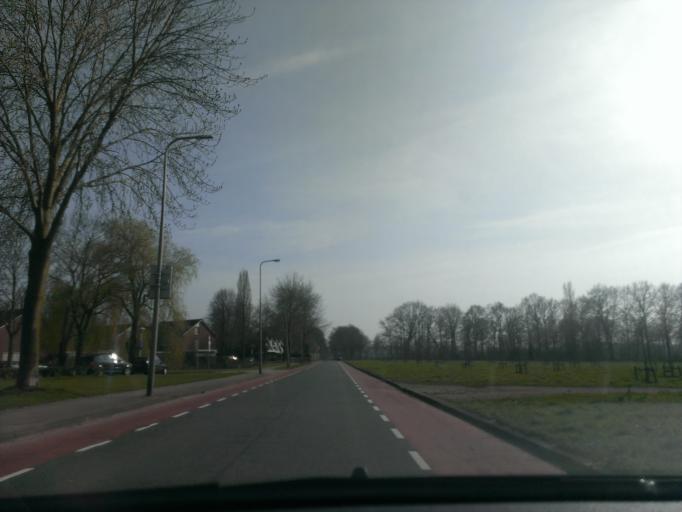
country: NL
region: Overijssel
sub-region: Gemeente Borne
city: Borne
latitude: 52.3051
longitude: 6.7349
